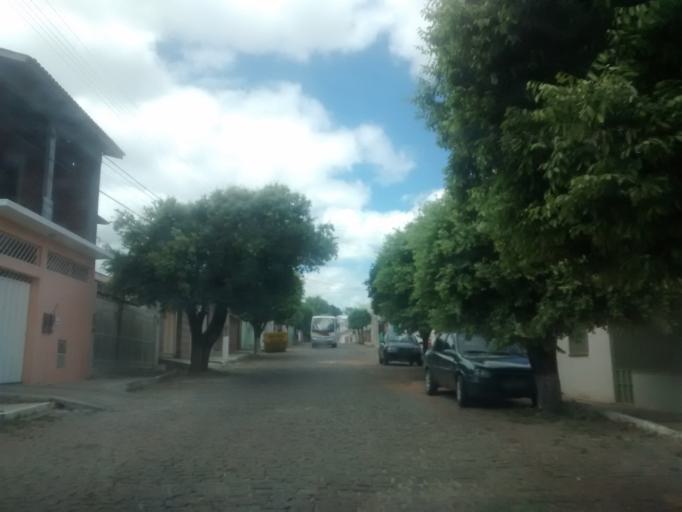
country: BR
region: Bahia
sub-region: Brumado
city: Brumado
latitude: -14.2011
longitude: -41.6720
